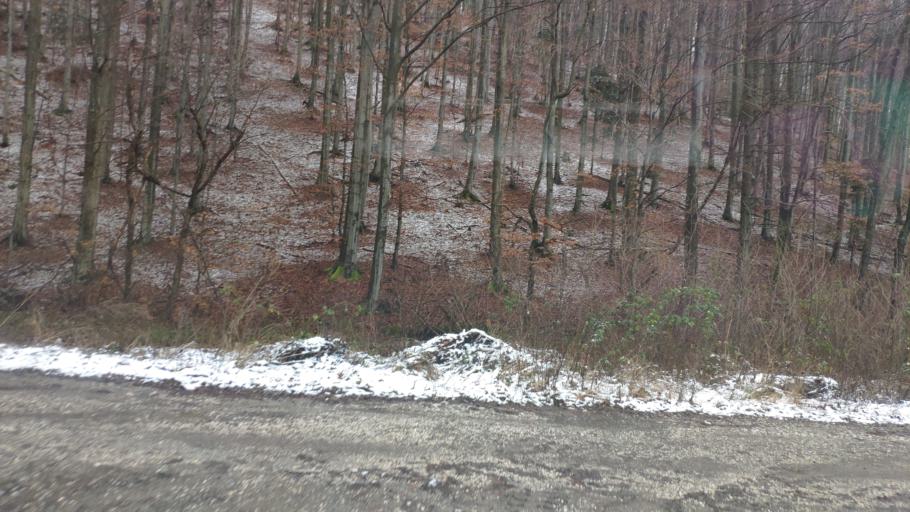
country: SK
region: Kosicky
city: Moldava nad Bodvou
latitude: 48.7397
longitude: 21.0641
